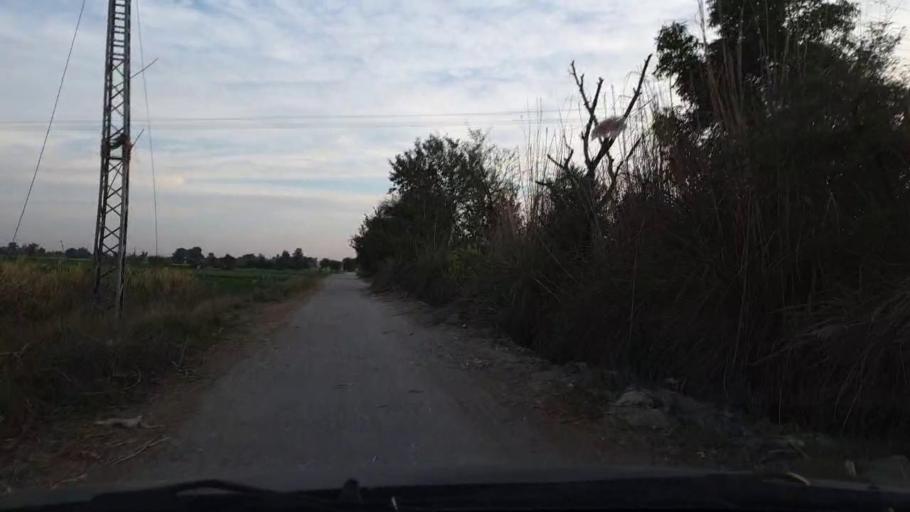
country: PK
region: Sindh
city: Khadro
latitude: 26.1250
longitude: 68.7780
